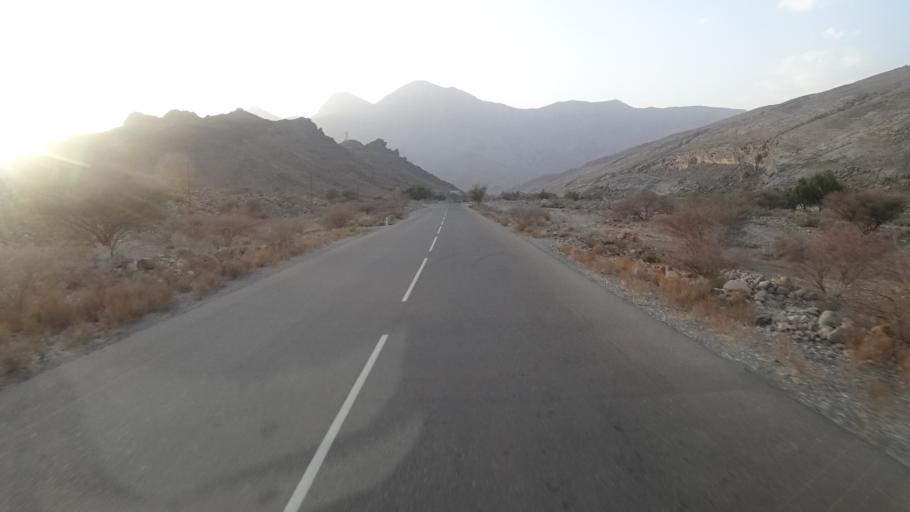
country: OM
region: Muhafazat ad Dakhiliyah
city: Bahla'
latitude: 23.1639
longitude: 57.1625
